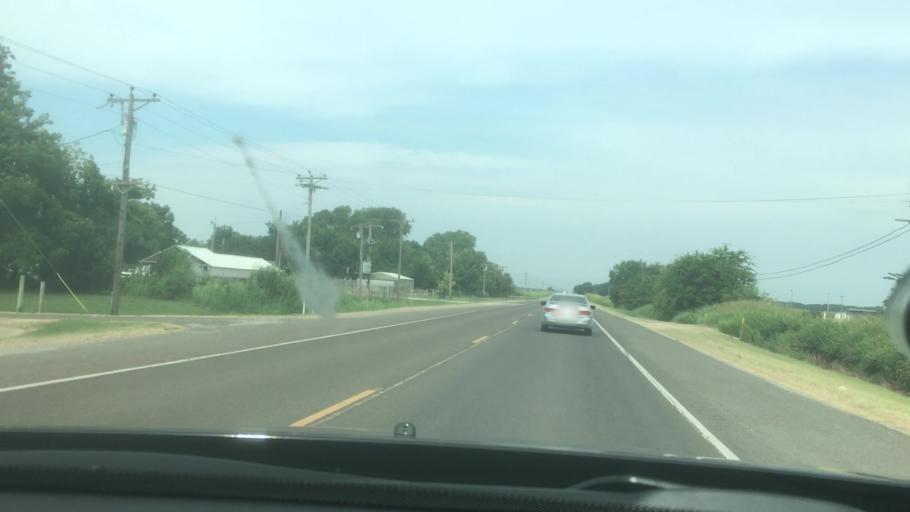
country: US
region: Oklahoma
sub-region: Garvin County
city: Maysville
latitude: 34.8192
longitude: -97.4537
